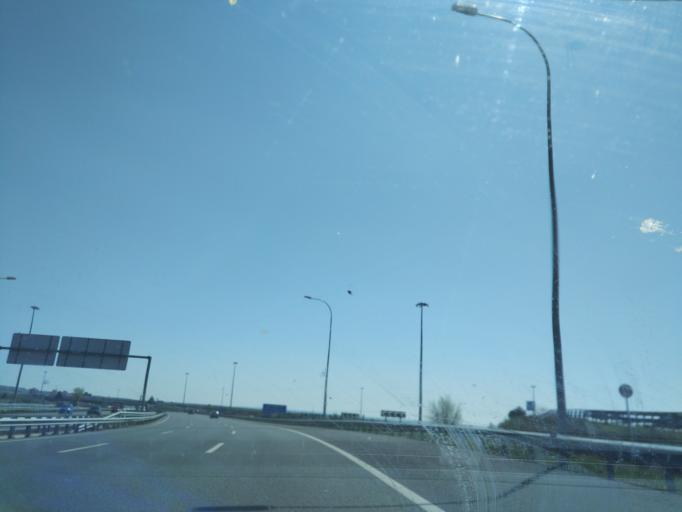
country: ES
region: Madrid
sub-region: Provincia de Madrid
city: Villa de Vallecas
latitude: 40.3617
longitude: -3.5703
